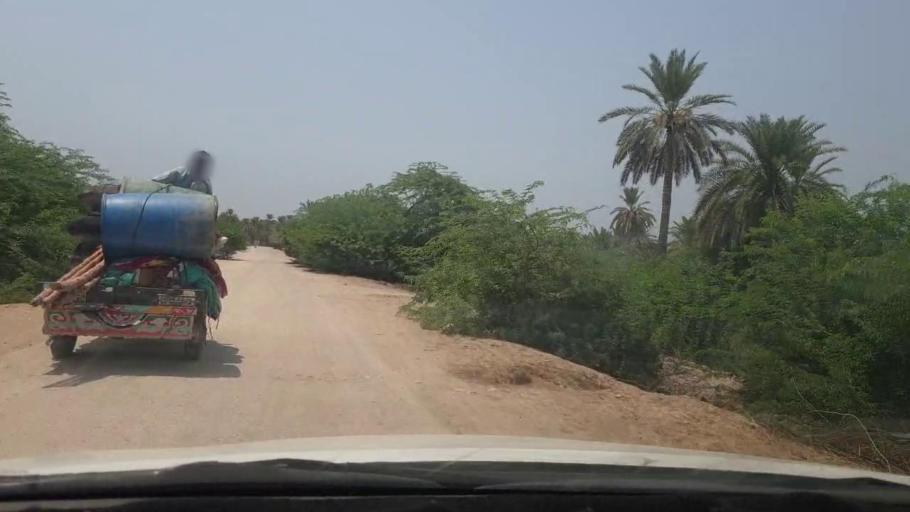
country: PK
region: Sindh
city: Khairpur
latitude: 27.4993
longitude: 68.8807
